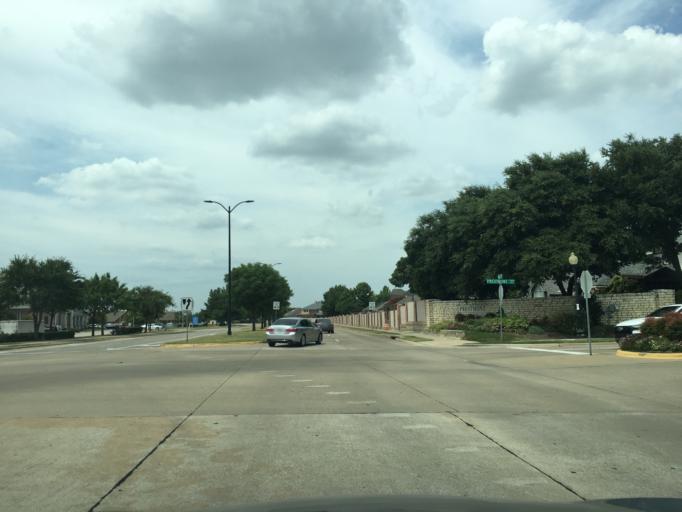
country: US
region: Texas
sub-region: Collin County
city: Frisco
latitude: 33.1112
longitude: -96.8011
